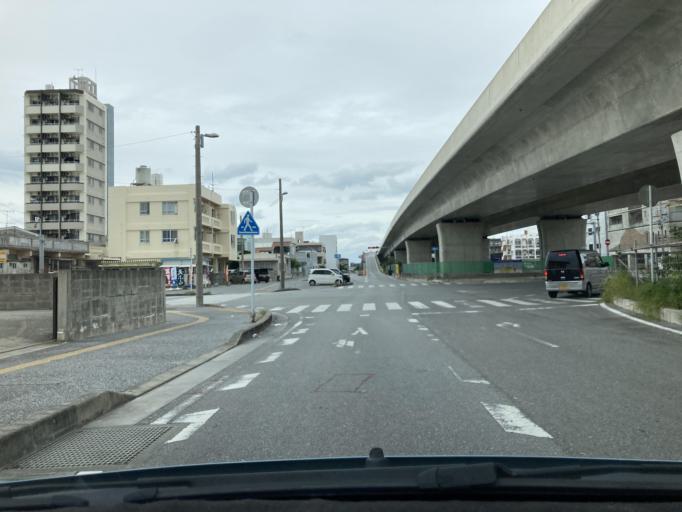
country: JP
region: Okinawa
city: Itoman
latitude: 26.1269
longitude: 127.6659
